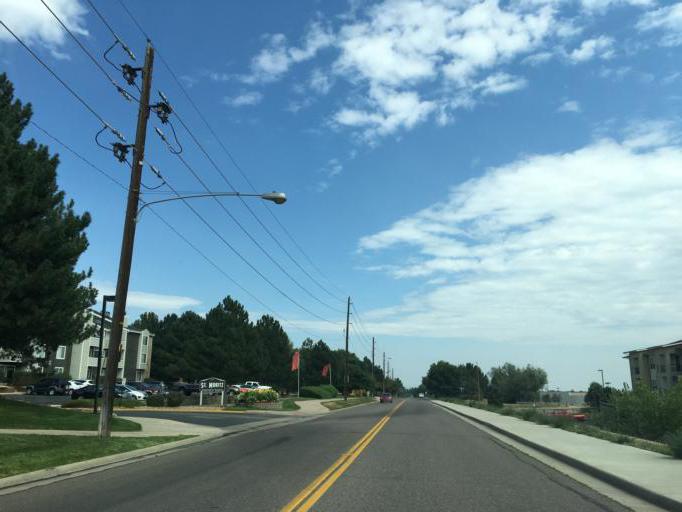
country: US
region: Colorado
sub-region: Jefferson County
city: Applewood
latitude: 39.7438
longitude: -105.1219
